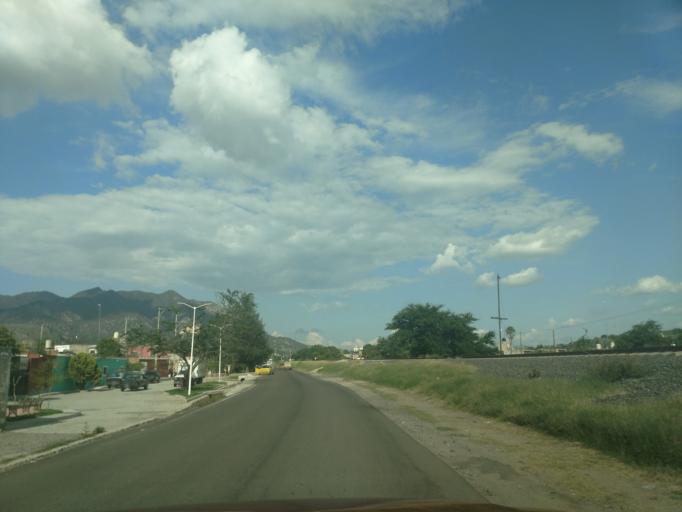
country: MX
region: Jalisco
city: Antonio Escobedo
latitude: 20.9051
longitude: -103.9821
